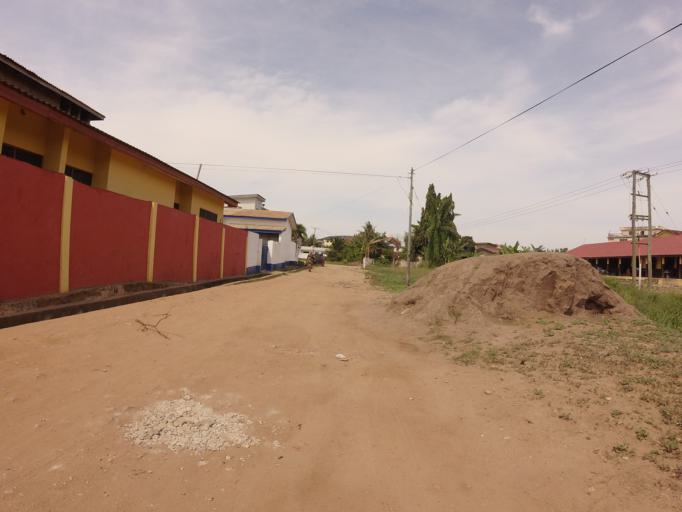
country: GH
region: Greater Accra
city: Dome
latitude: 5.6269
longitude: -0.2320
